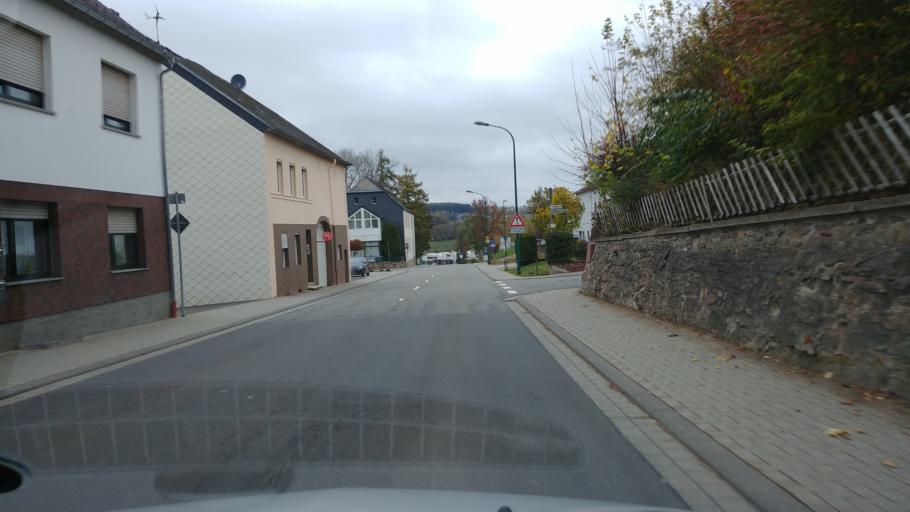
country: DE
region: Rheinland-Pfalz
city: Hermeskeil
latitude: 49.6598
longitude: 6.9497
